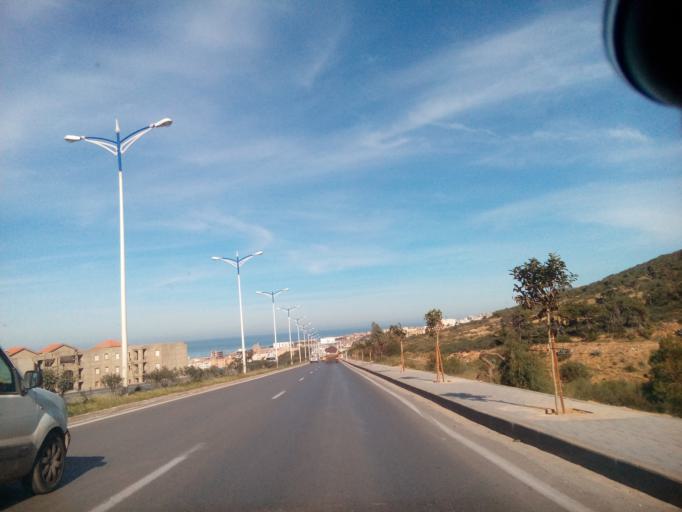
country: DZ
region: Mostaganem
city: Mostaganem
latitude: 35.9489
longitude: 0.0997
